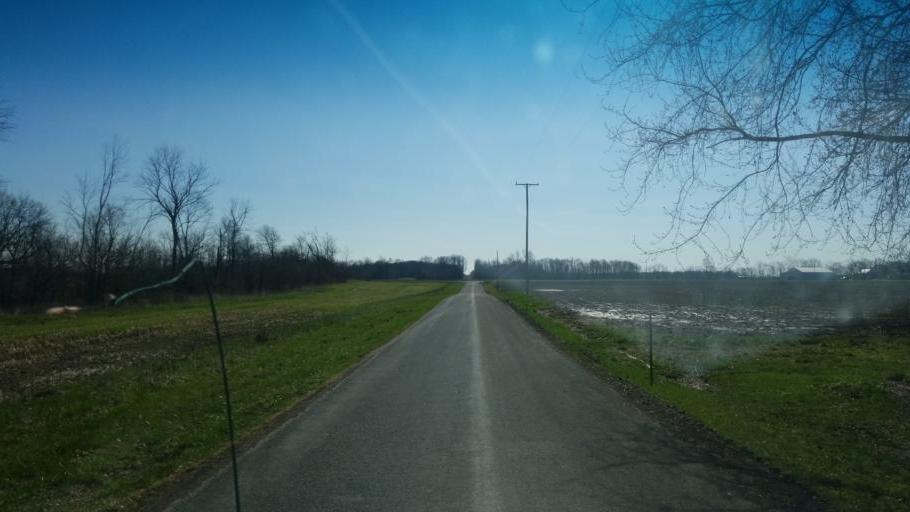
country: US
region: Ohio
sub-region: Hardin County
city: Forest
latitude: 40.7015
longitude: -83.4999
